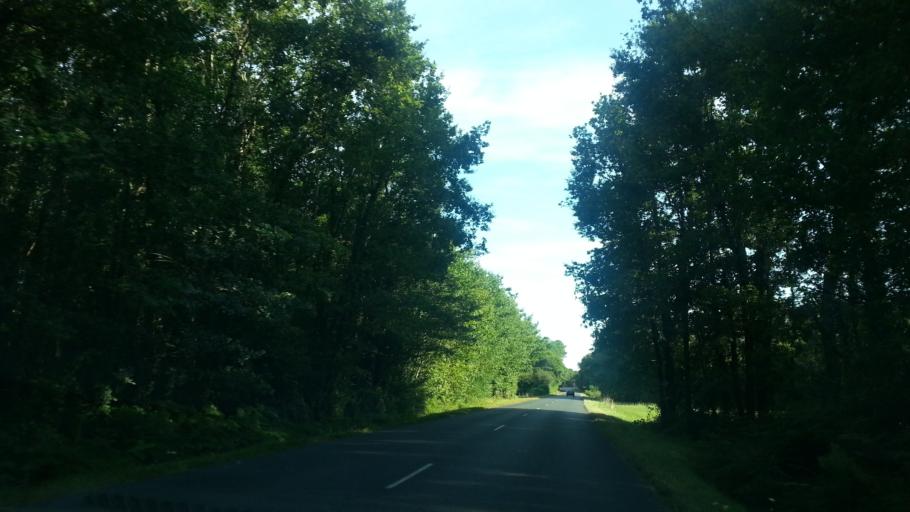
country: FR
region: Aquitaine
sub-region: Departement de la Gironde
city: Illats
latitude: 44.6180
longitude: -0.3724
